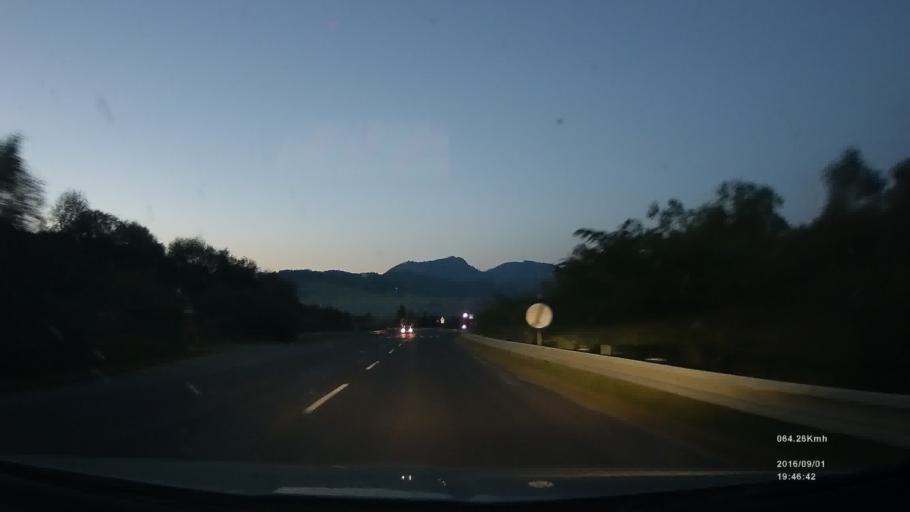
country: SK
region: Zilinsky
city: Ruzomberok
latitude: 49.0918
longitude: 19.4351
